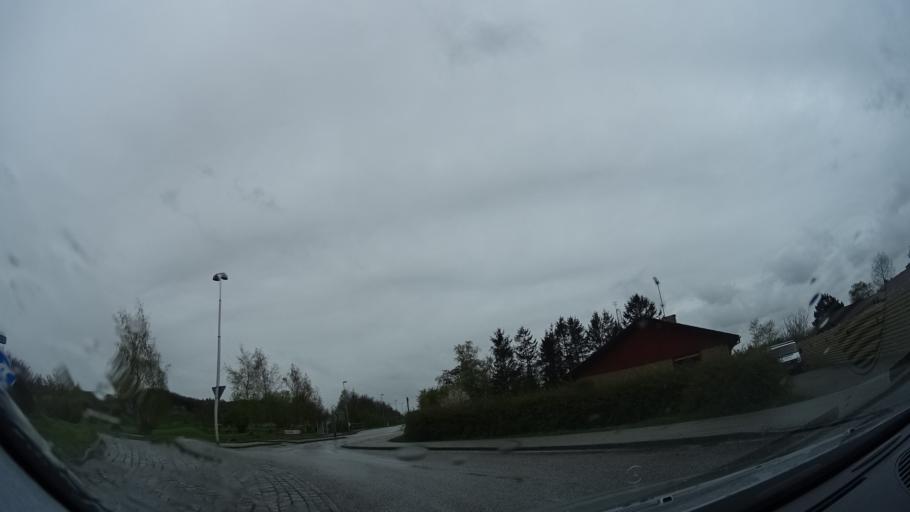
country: DK
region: Zealand
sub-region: Lejre Kommune
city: Ejby
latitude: 55.6874
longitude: 11.8517
